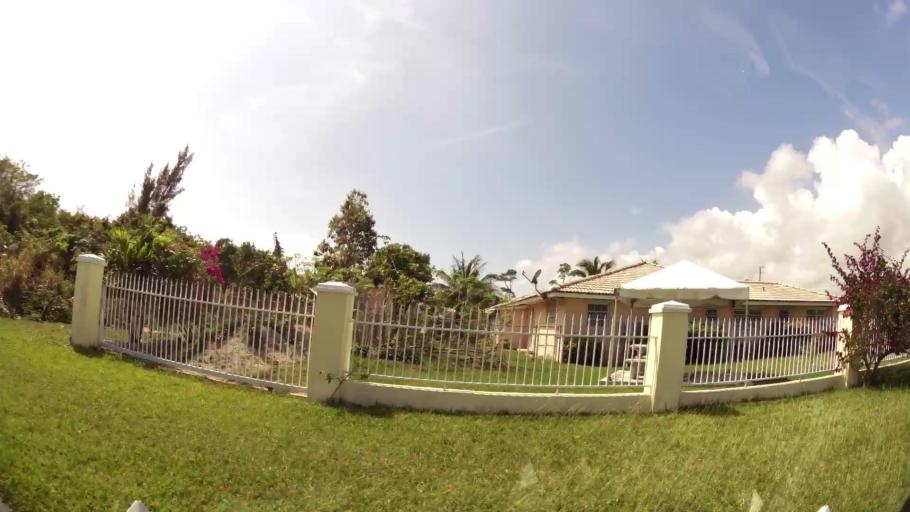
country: BS
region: Freeport
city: Freeport
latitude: 26.5011
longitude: -78.7028
